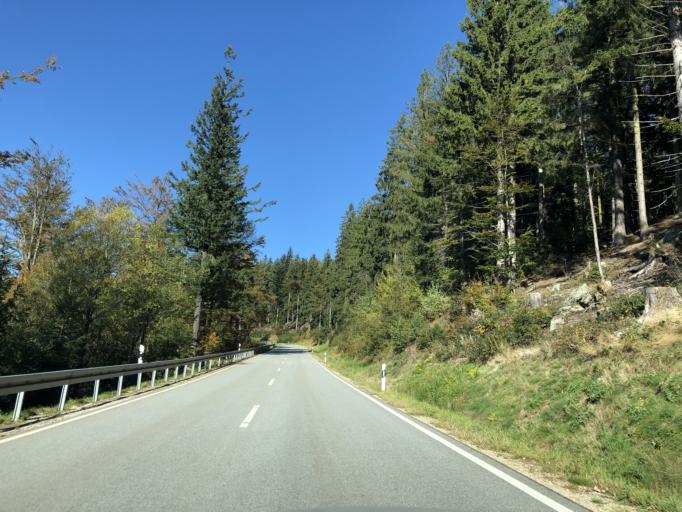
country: DE
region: Bavaria
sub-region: Lower Bavaria
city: Bodenmais
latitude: 49.0680
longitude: 13.1337
